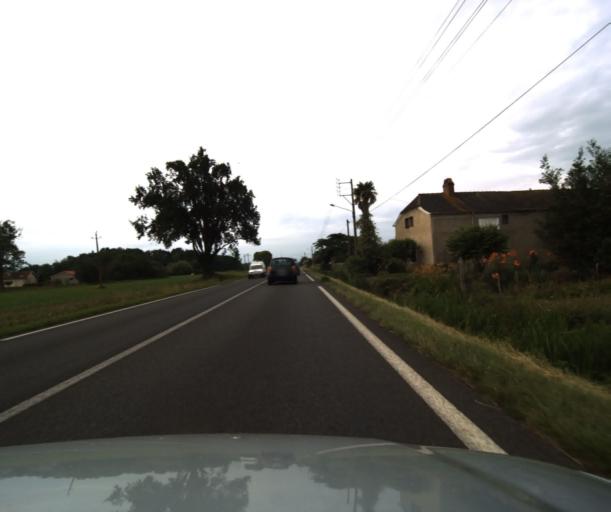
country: FR
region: Midi-Pyrenees
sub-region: Departement des Hautes-Pyrenees
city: Rabastens-de-Bigorre
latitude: 43.3368
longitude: 0.1314
